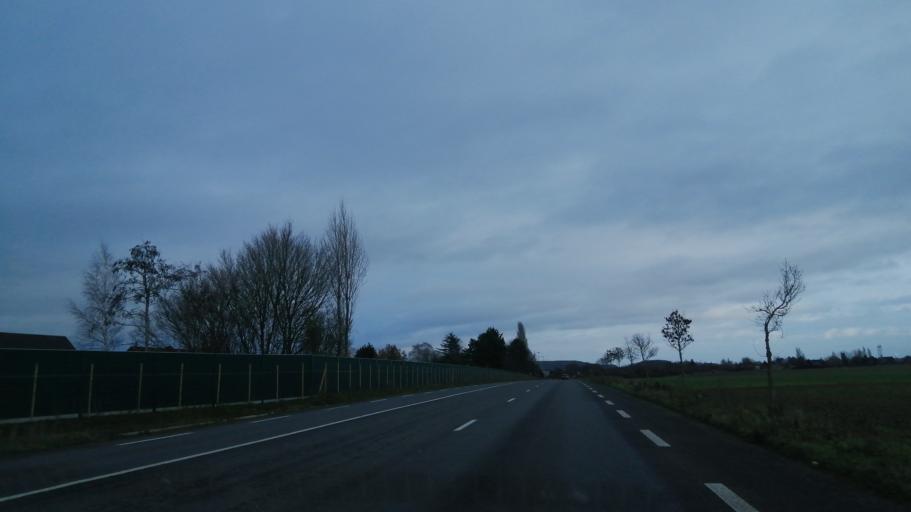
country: FR
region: Nord-Pas-de-Calais
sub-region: Departement du Pas-de-Calais
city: Mericourt
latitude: 50.3959
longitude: 2.8777
